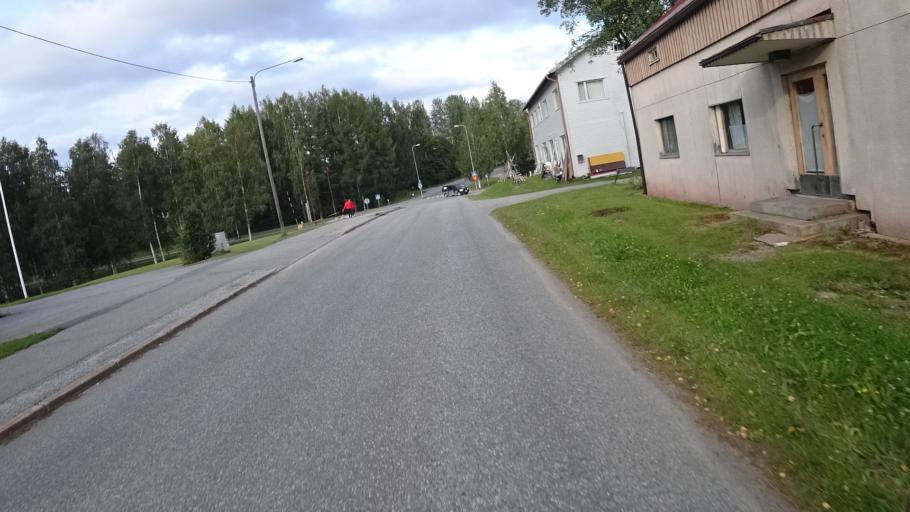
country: FI
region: North Karelia
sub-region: Joensuu
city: Ilomantsi
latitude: 62.6735
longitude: 30.9272
